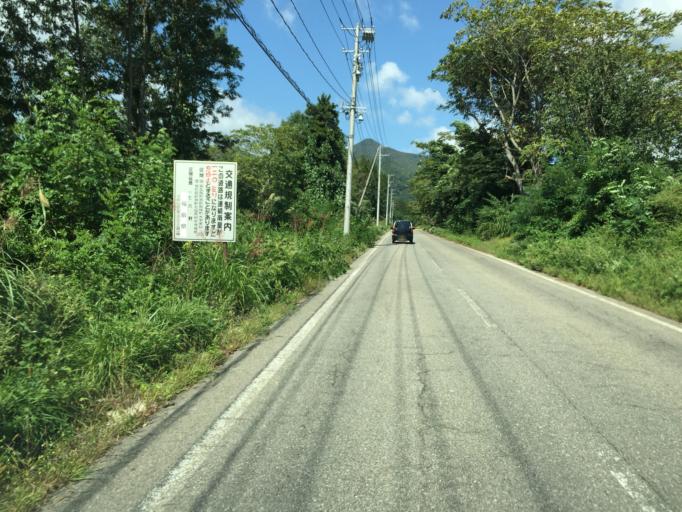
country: JP
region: Fukushima
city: Inawashiro
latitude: 37.5703
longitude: 140.0189
